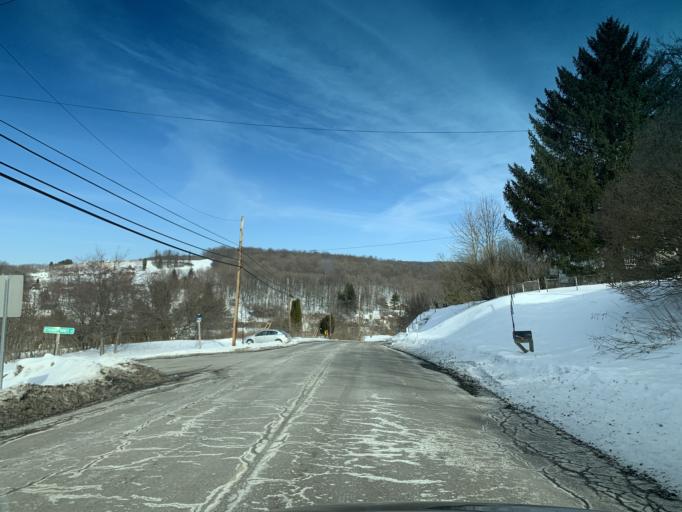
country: US
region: Maryland
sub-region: Allegany County
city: Frostburg
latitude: 39.6505
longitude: -78.8994
